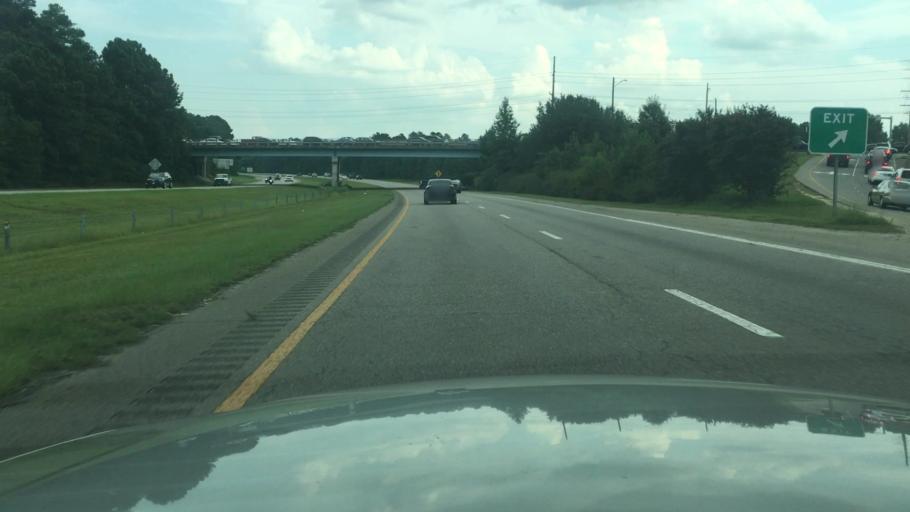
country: US
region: North Carolina
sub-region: Cumberland County
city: Fayetteville
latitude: 35.0607
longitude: -78.9547
